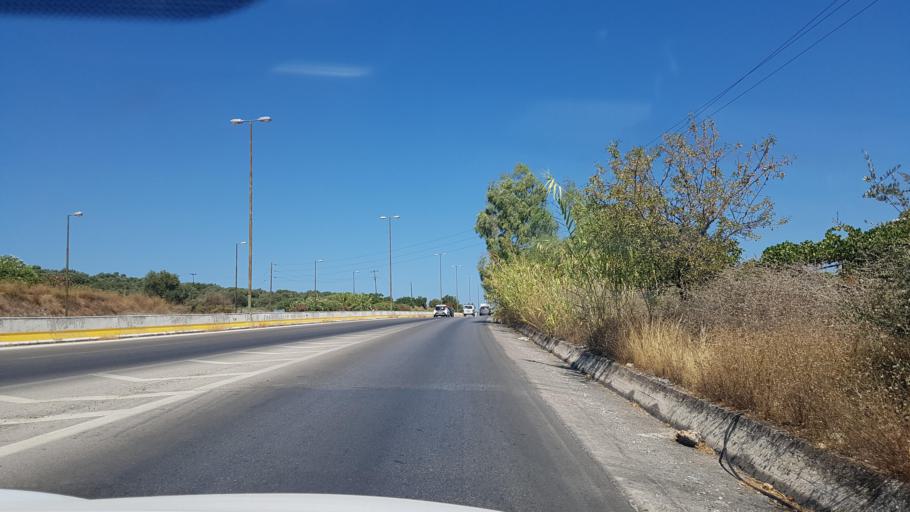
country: GR
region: Crete
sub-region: Nomos Chanias
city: Perivolia
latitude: 35.4991
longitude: 23.9912
